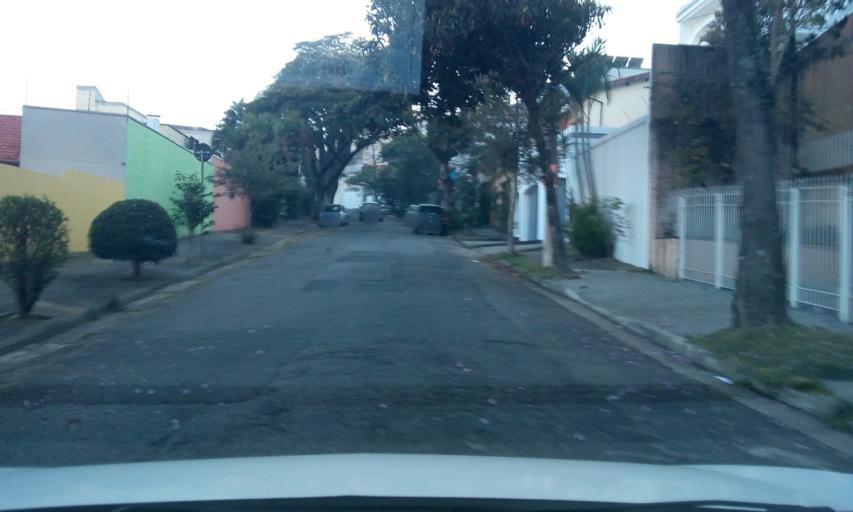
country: BR
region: Sao Paulo
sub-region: Sao Paulo
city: Sao Paulo
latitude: -23.5376
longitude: -46.6984
